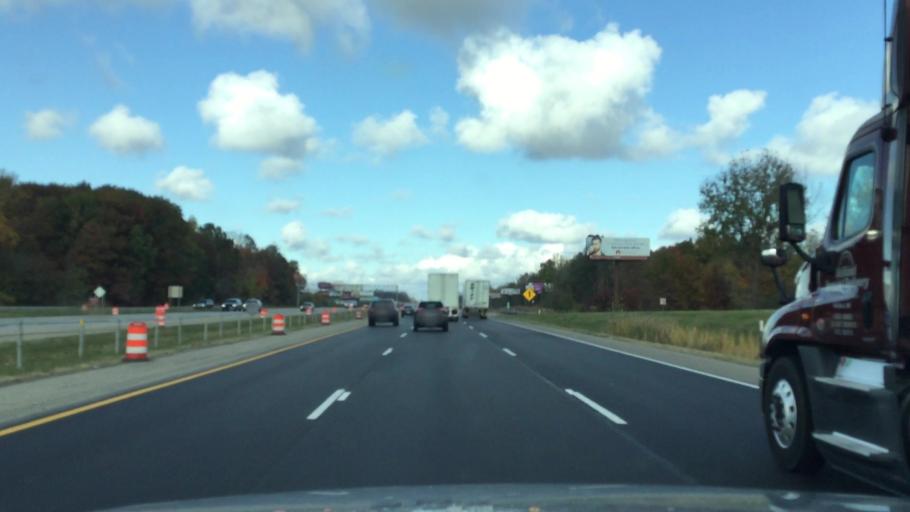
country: US
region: Michigan
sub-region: Berrien County
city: Benton Heights
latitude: 42.0913
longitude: -86.4086
